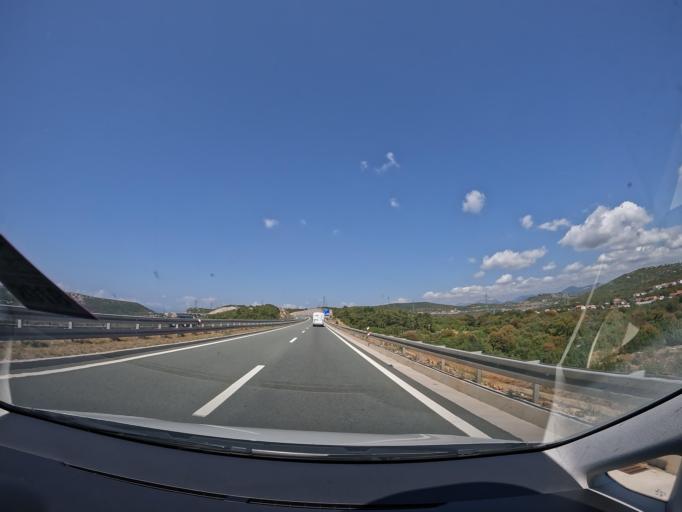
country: HR
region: Primorsko-Goranska
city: Krasica
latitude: 45.3103
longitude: 14.5531
